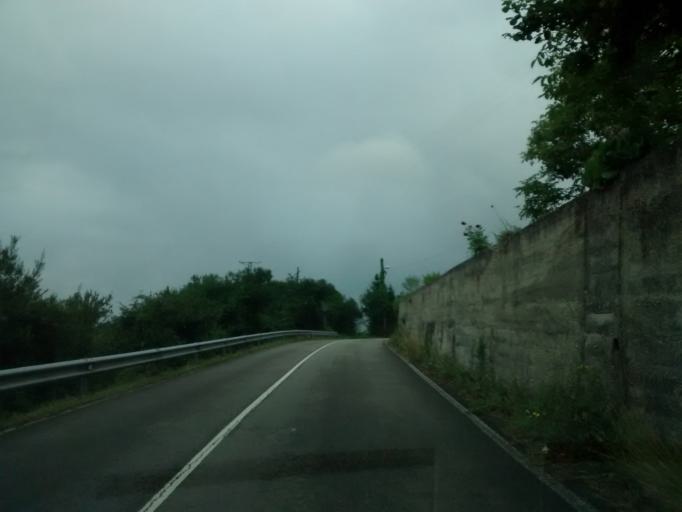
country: ES
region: Asturias
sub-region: Province of Asturias
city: Villaviciosa
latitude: 43.5191
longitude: -5.3711
